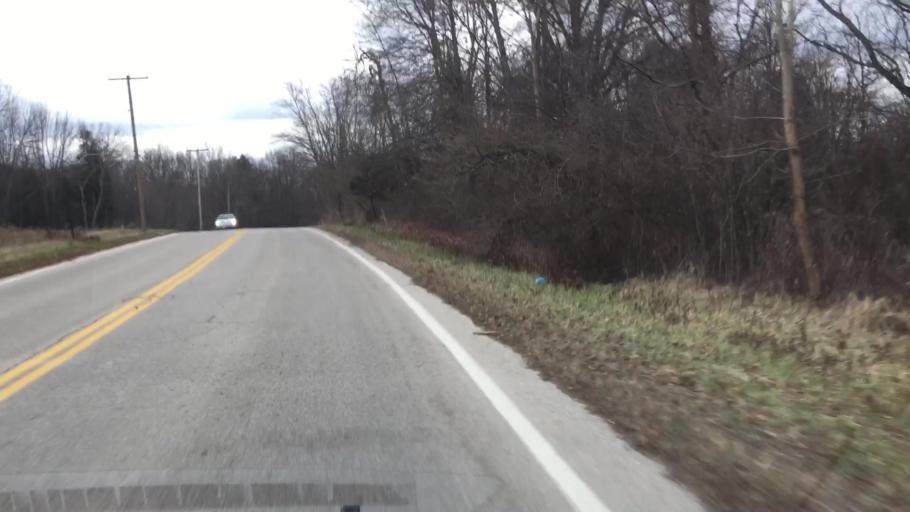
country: US
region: Ohio
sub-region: Summit County
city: Silver Lake
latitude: 41.1991
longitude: -81.4722
